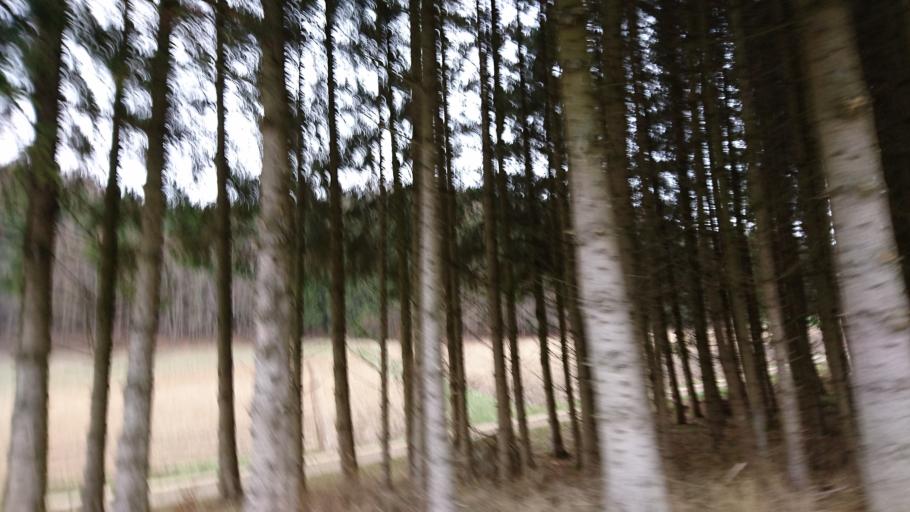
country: DE
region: Bavaria
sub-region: Swabia
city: Zusmarshausen
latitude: 48.4299
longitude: 10.6119
